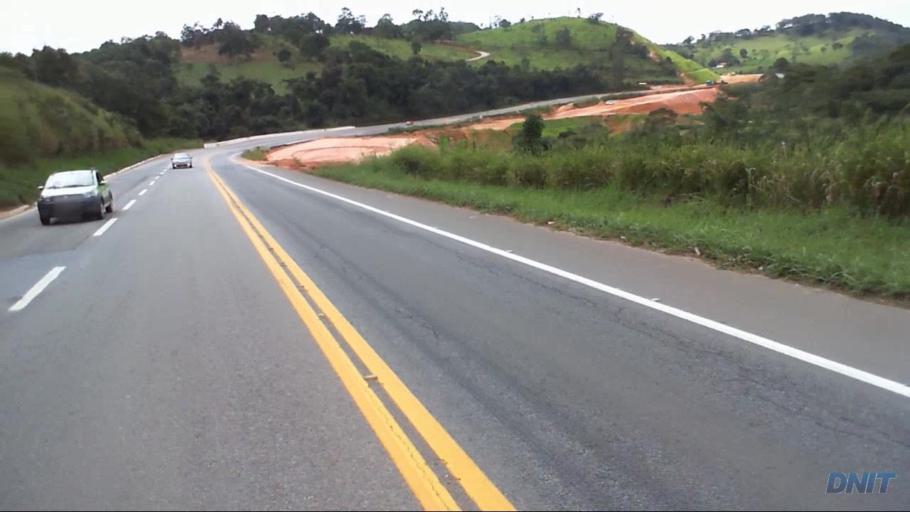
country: BR
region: Minas Gerais
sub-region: Caete
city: Caete
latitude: -19.7487
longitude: -43.6250
